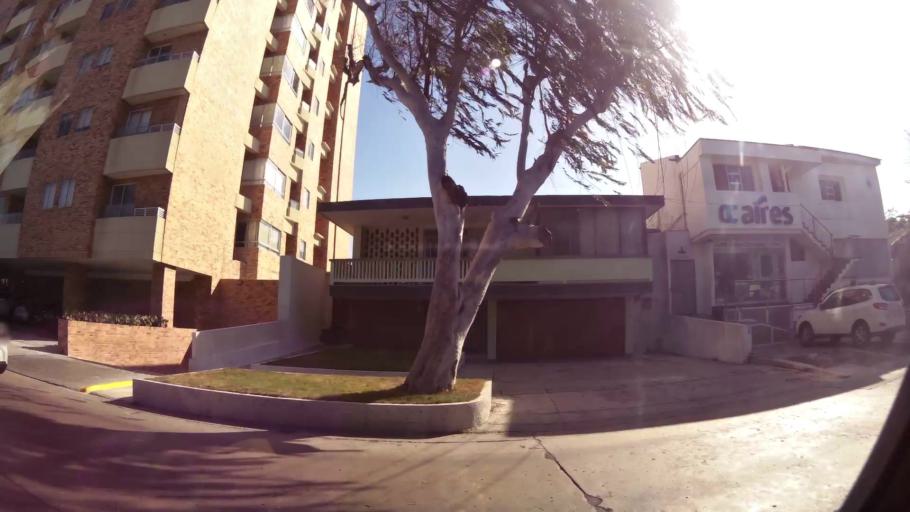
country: CO
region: Atlantico
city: Barranquilla
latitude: 10.9981
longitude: -74.8222
